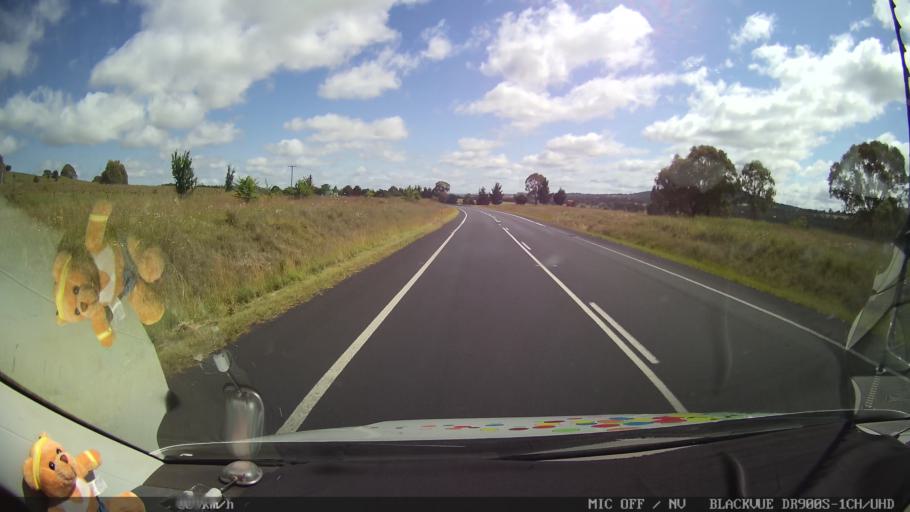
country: AU
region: New South Wales
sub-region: Glen Innes Severn
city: Glen Innes
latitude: -29.8870
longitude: 151.7335
